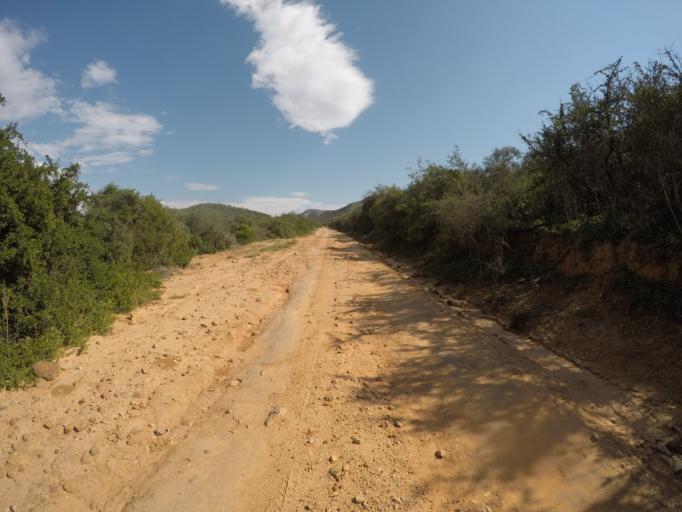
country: ZA
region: Eastern Cape
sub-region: Cacadu District Municipality
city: Kareedouw
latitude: -33.6547
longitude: 24.4162
